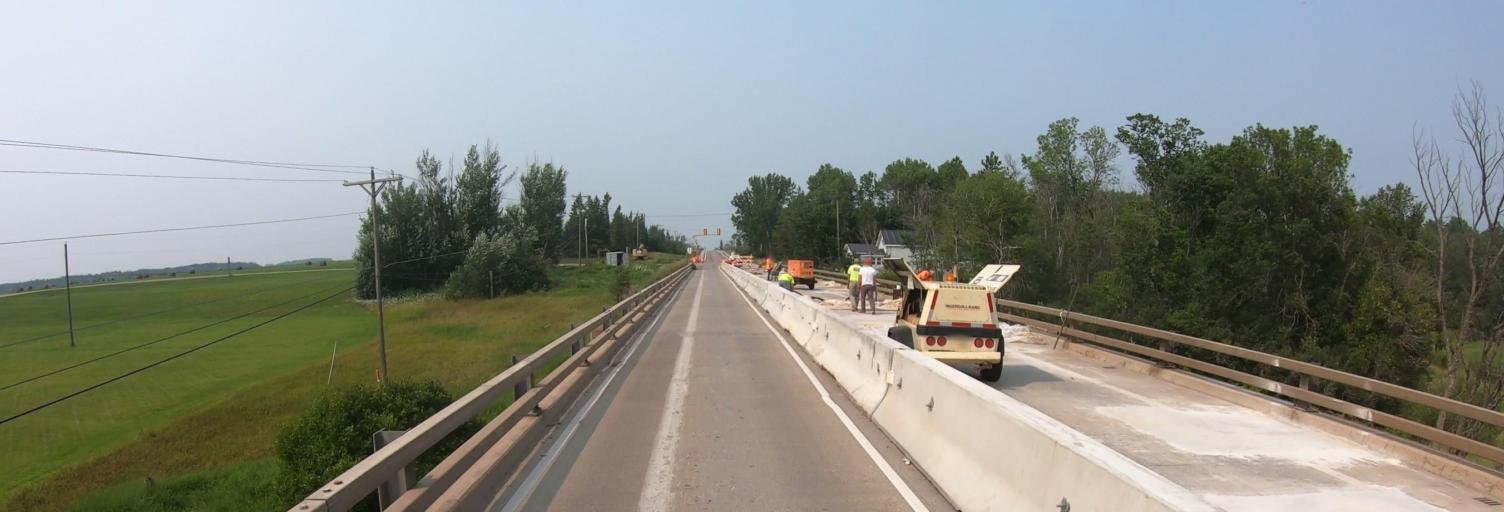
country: US
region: Michigan
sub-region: Chippewa County
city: Sault Ste. Marie
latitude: 46.1429
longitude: -84.3634
